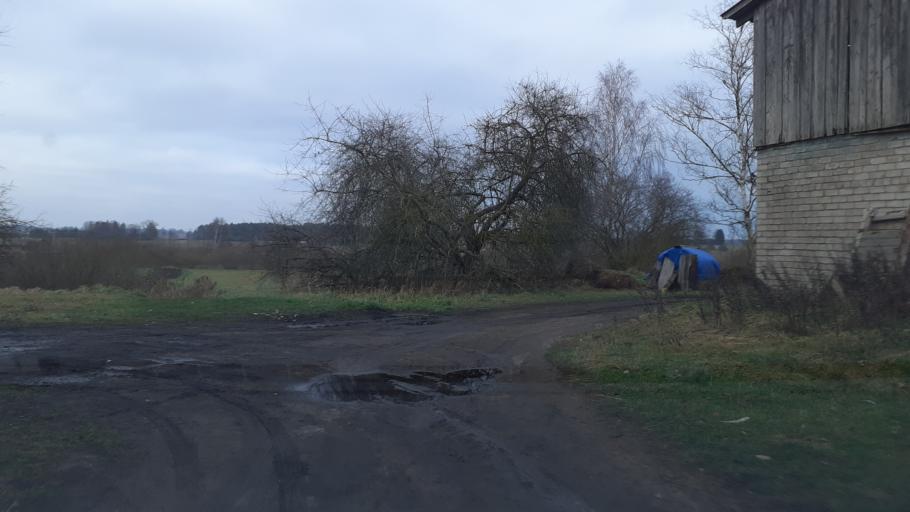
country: LV
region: Aizpute
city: Aizpute
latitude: 56.8000
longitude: 21.6708
